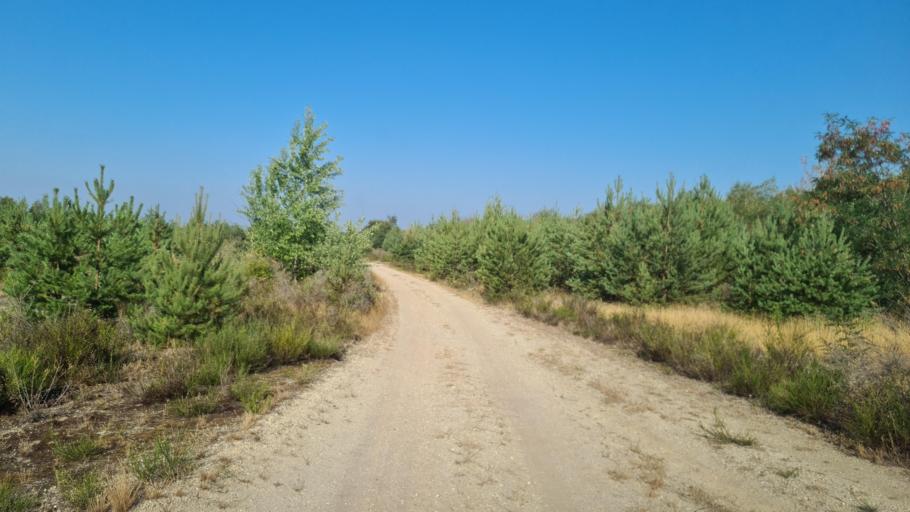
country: DE
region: Brandenburg
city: Sallgast
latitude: 51.5655
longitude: 13.8317
